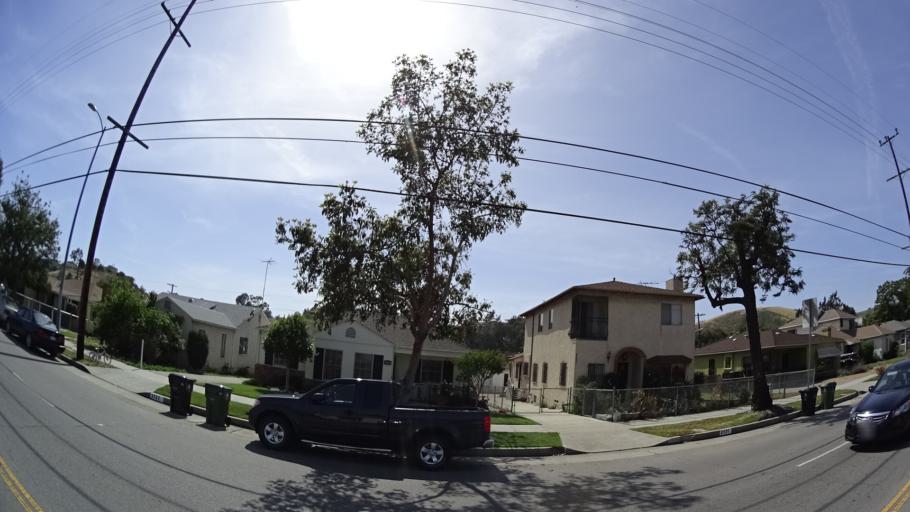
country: US
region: California
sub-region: Los Angeles County
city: Belvedere
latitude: 34.0686
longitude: -118.1804
